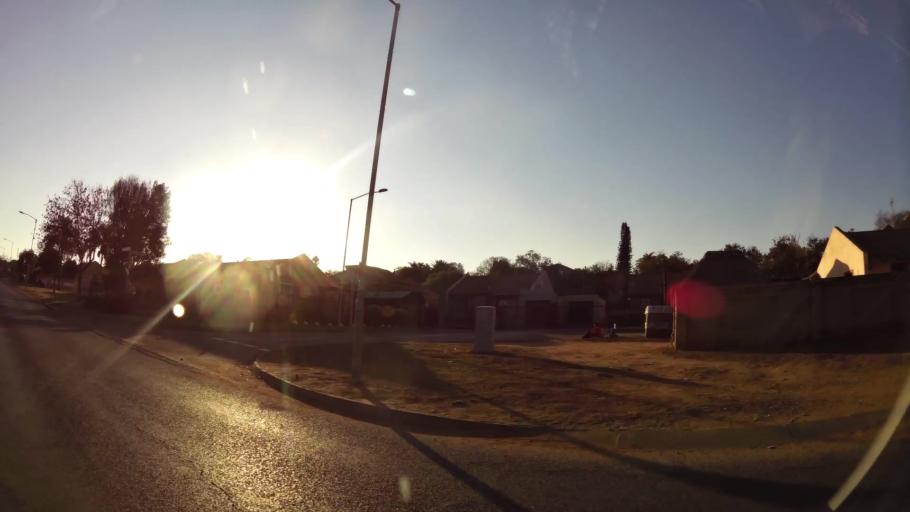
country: ZA
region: Gauteng
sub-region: City of Tshwane Metropolitan Municipality
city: Pretoria
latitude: -25.7388
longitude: 28.1125
